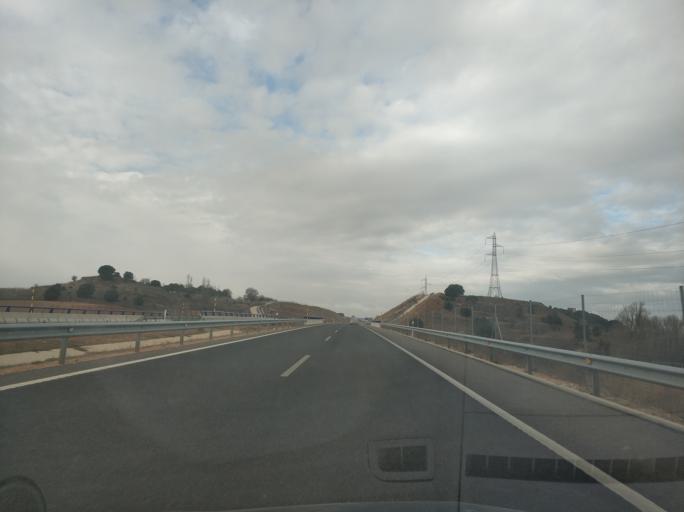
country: ES
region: Castille and Leon
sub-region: Provincia de Burgos
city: Fresnillo de las Duenas
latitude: 41.6394
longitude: -3.6618
